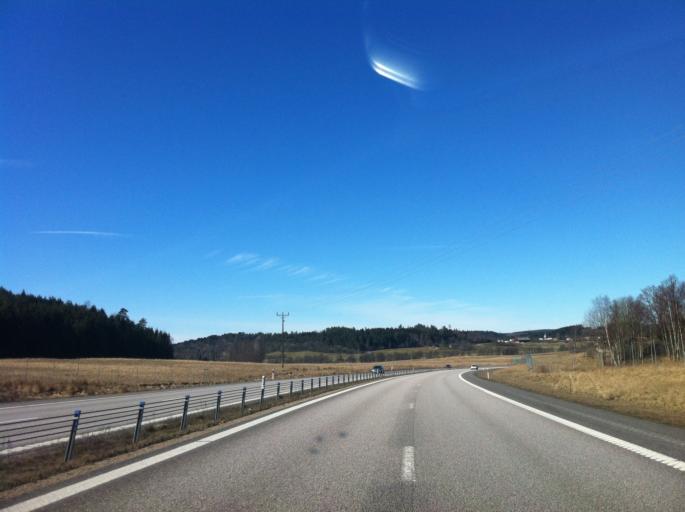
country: SE
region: Vaestra Goetaland
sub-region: Munkedals Kommun
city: Munkedal
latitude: 58.4010
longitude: 11.7452
